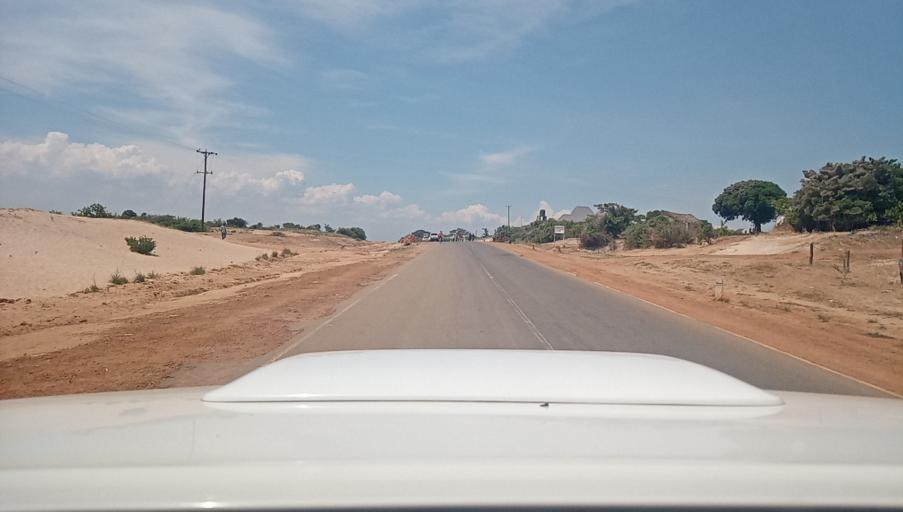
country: ZM
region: Luapula
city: Samfya
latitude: -11.3518
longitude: 29.5581
